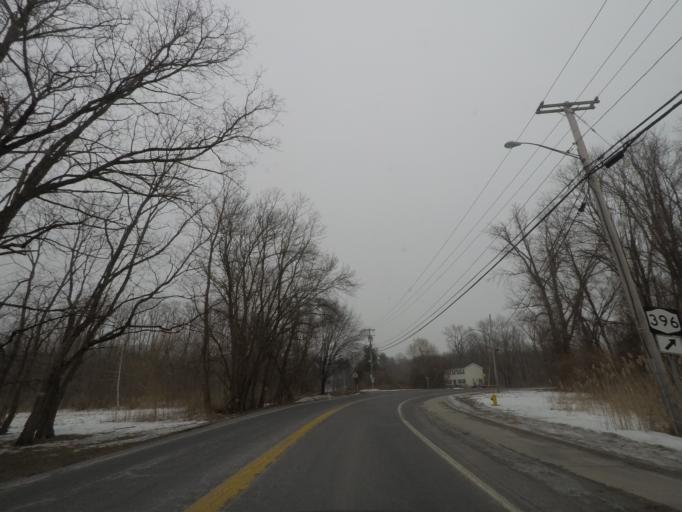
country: US
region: New York
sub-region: Rensselaer County
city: Castleton-on-Hudson
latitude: 42.5462
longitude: -73.8030
